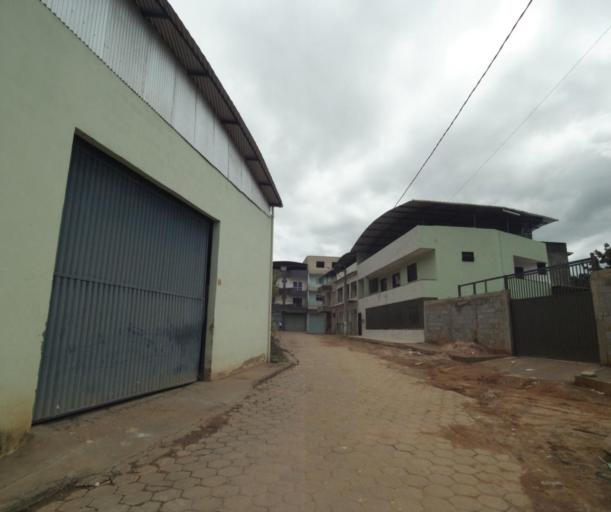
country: BR
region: Espirito Santo
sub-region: Irupi
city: Irupi
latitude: -20.3456
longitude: -41.6391
